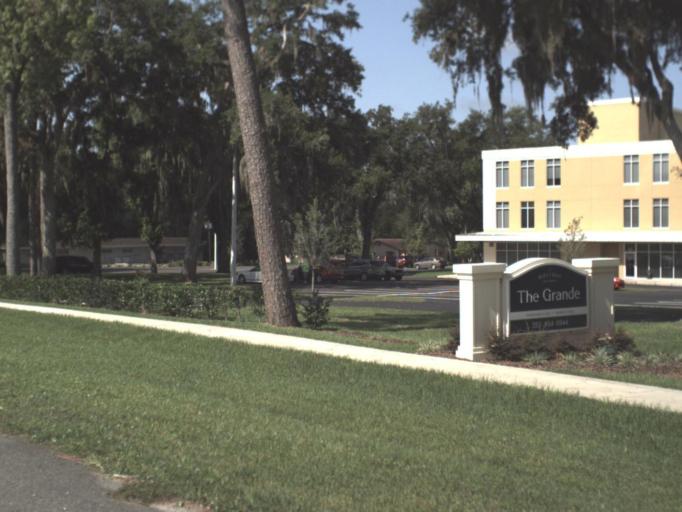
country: US
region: Florida
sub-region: Hernando County
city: Brooksville
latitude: 28.5534
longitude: -82.3977
